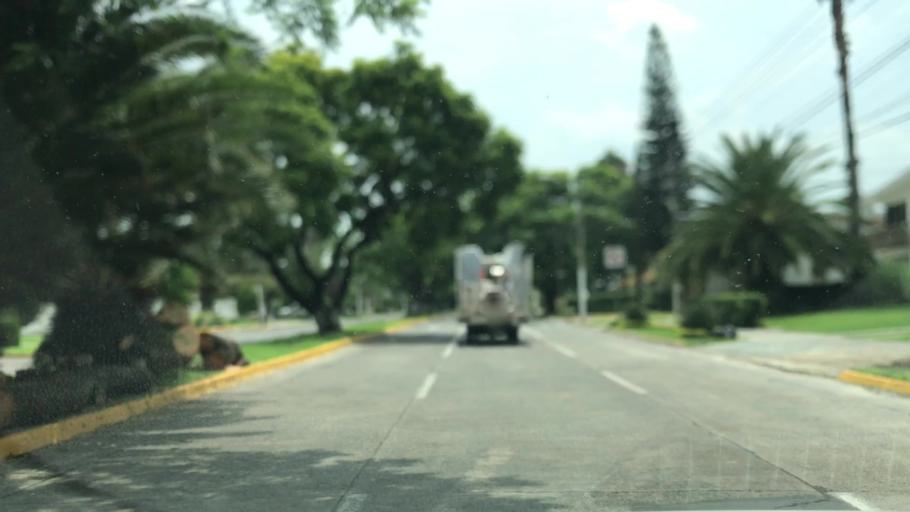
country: MX
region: Jalisco
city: Guadalajara
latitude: 20.6505
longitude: -103.4156
